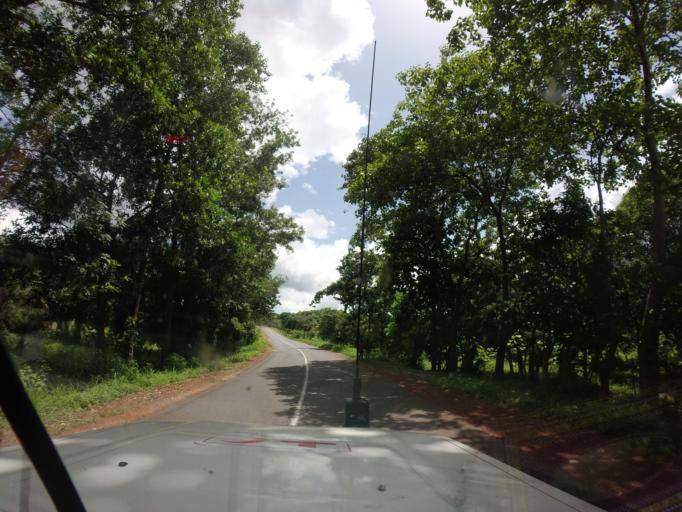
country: SL
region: Northern Province
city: Bindi
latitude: 10.1475
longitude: -11.6169
